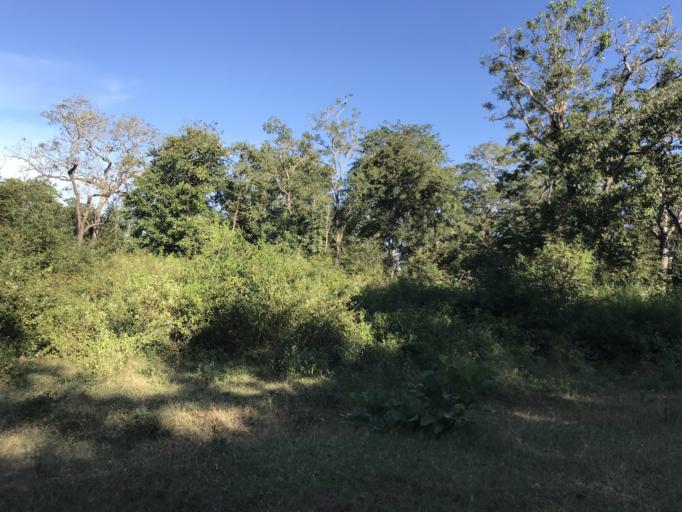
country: IN
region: Karnataka
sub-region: Mysore
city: Heggadadevankote
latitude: 11.9747
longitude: 76.2415
